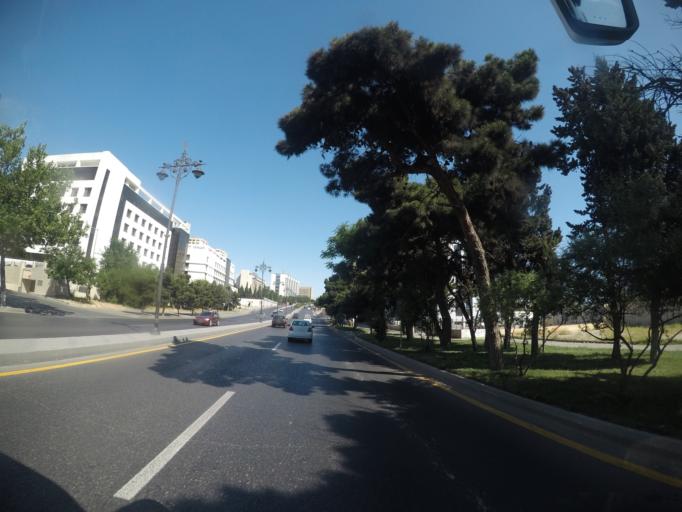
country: AZ
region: Baki
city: Khodzhi-Gasan
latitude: 40.3990
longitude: 49.8121
